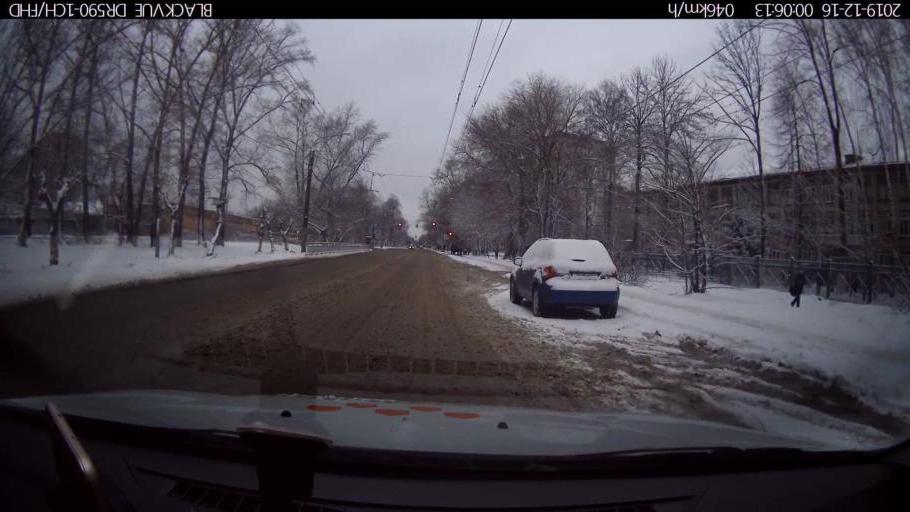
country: RU
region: Nizjnij Novgorod
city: Nizhniy Novgorod
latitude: 56.2710
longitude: 43.9385
